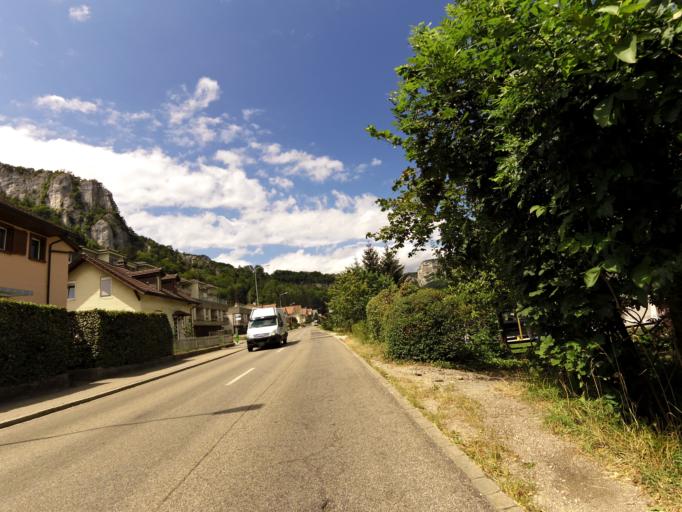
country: CH
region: Solothurn
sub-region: Bezirk Gaeu
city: Oensingen
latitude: 47.2875
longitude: 7.7061
